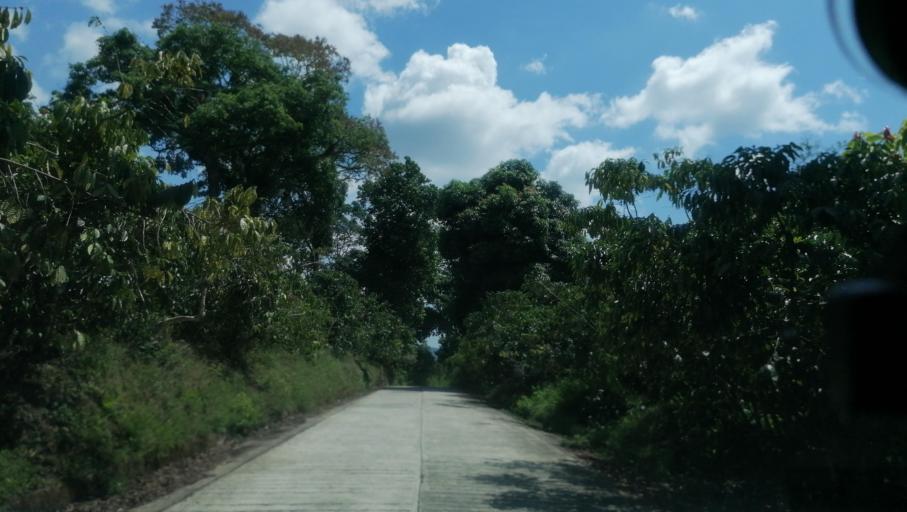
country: MX
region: Chiapas
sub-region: Union Juarez
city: Santo Domingo
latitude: 15.0414
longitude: -92.1452
